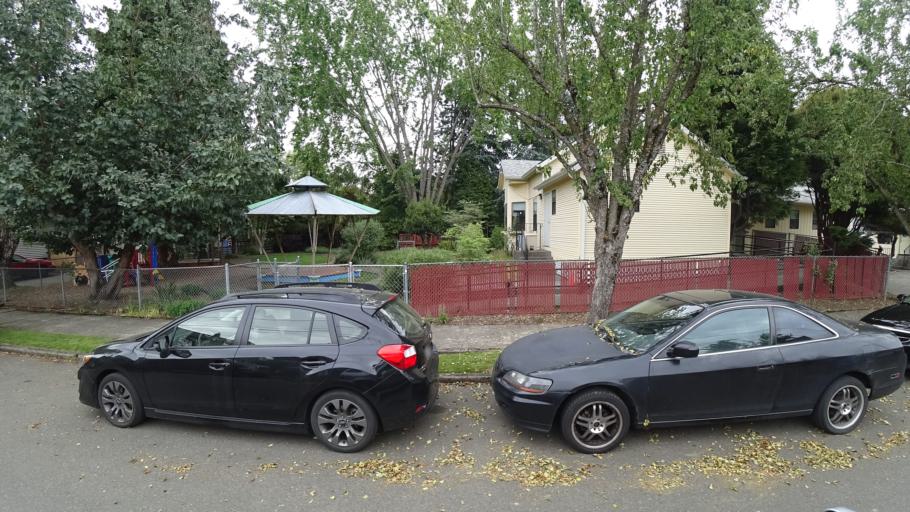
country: US
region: Oregon
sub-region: Multnomah County
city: Portland
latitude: 45.5479
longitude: -122.6599
